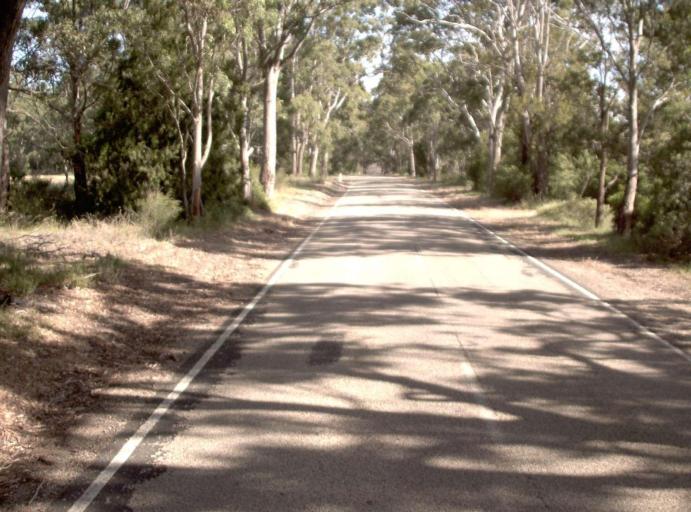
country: AU
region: Victoria
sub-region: East Gippsland
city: Lakes Entrance
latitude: -37.7957
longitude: 147.8319
